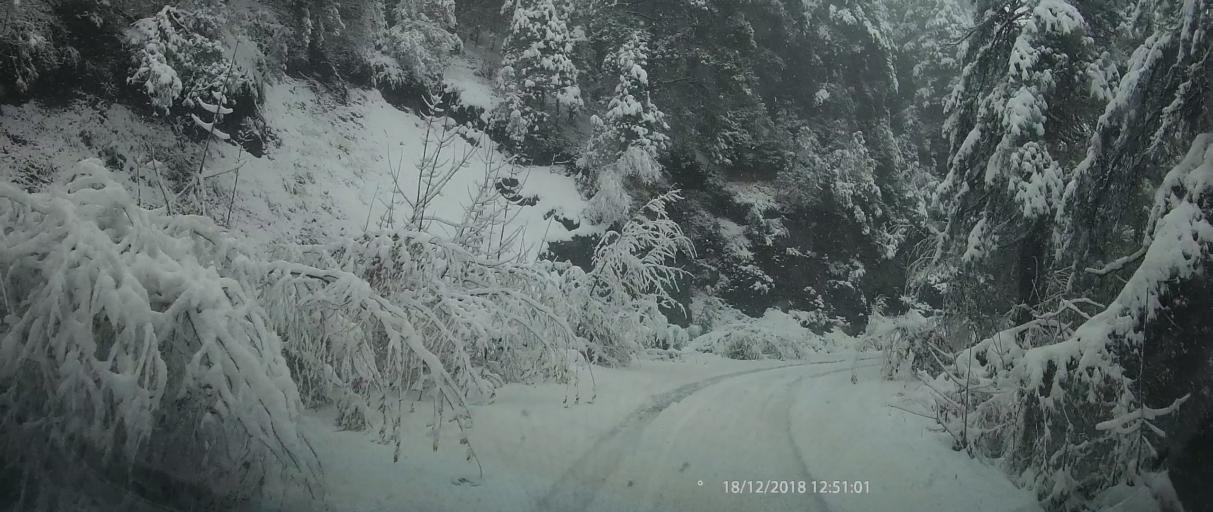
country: GR
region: Central Macedonia
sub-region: Nomos Pierias
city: Litochoro
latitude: 40.1032
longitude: 22.4467
